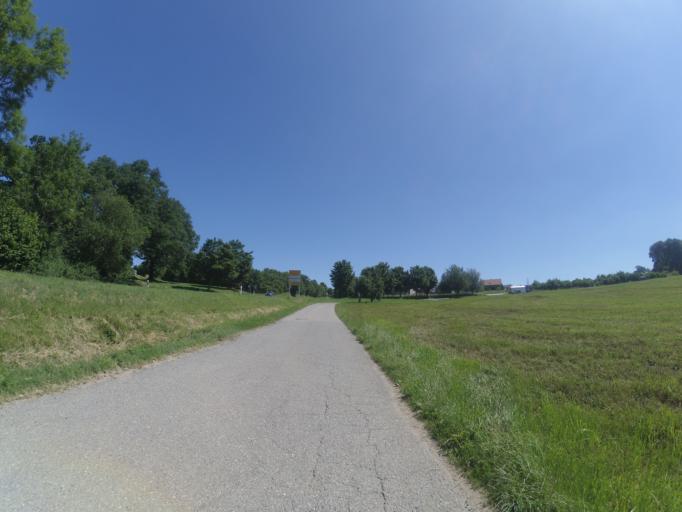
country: DE
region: Baden-Wuerttemberg
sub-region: Tuebingen Region
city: Bad Wurzach
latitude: 47.9017
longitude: 9.9026
